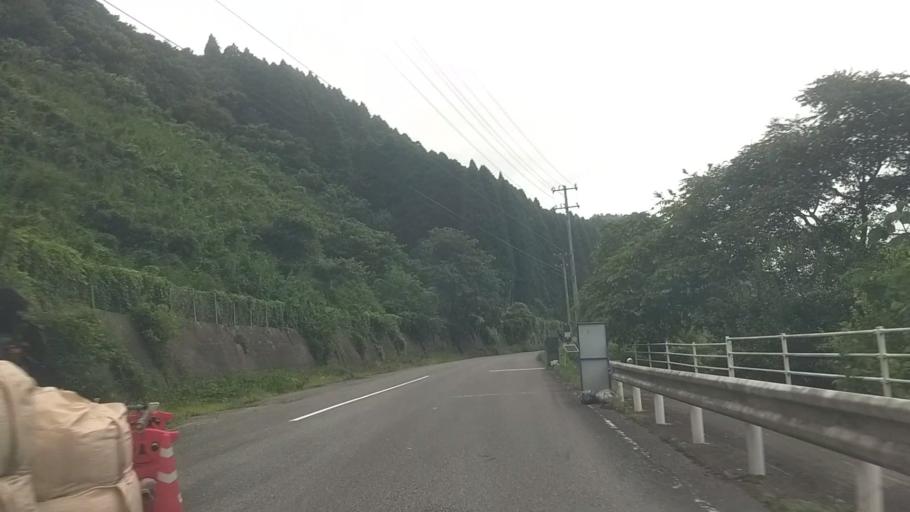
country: JP
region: Chiba
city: Katsuura
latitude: 35.2571
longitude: 140.2441
